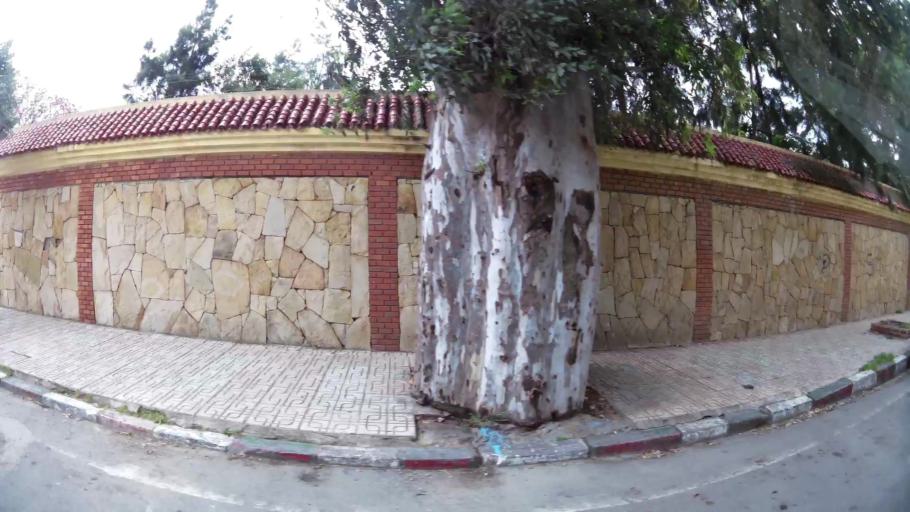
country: MA
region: Tanger-Tetouan
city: Tetouan
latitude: 35.5727
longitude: -5.3522
